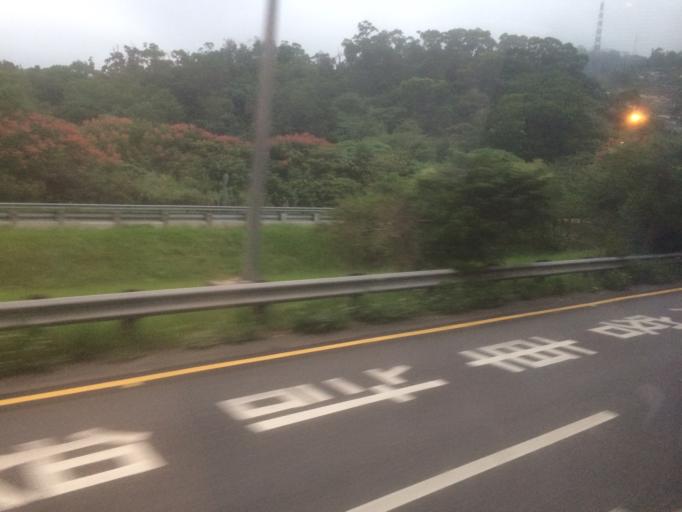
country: TW
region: Taipei
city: Taipei
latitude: 25.0069
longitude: 121.5813
